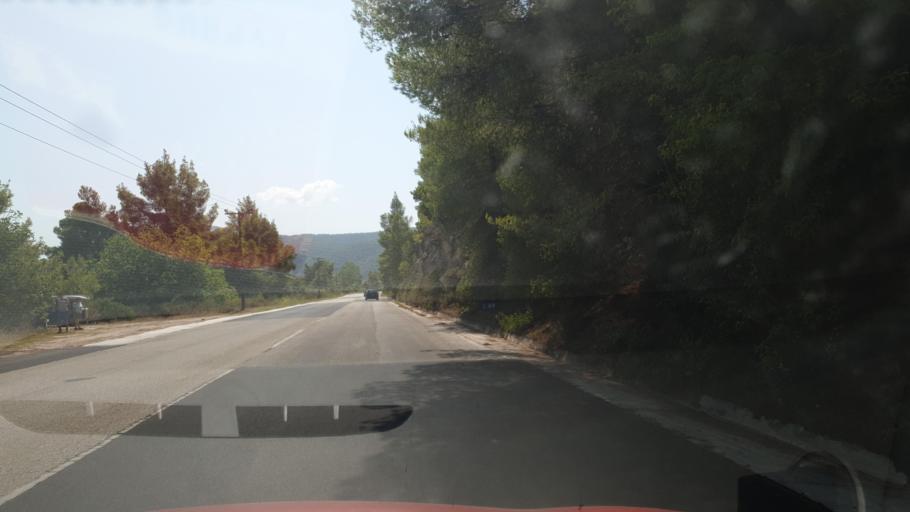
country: GR
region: Central Macedonia
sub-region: Nomos Chalkidikis
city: Agios Nikolaos
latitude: 40.2001
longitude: 23.7649
